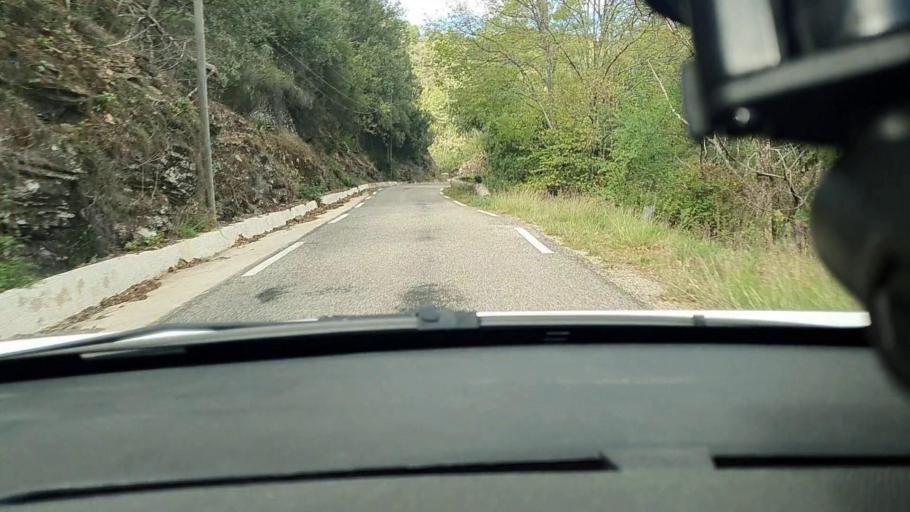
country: FR
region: Languedoc-Roussillon
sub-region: Departement du Gard
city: Besseges
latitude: 44.3006
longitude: 4.0381
